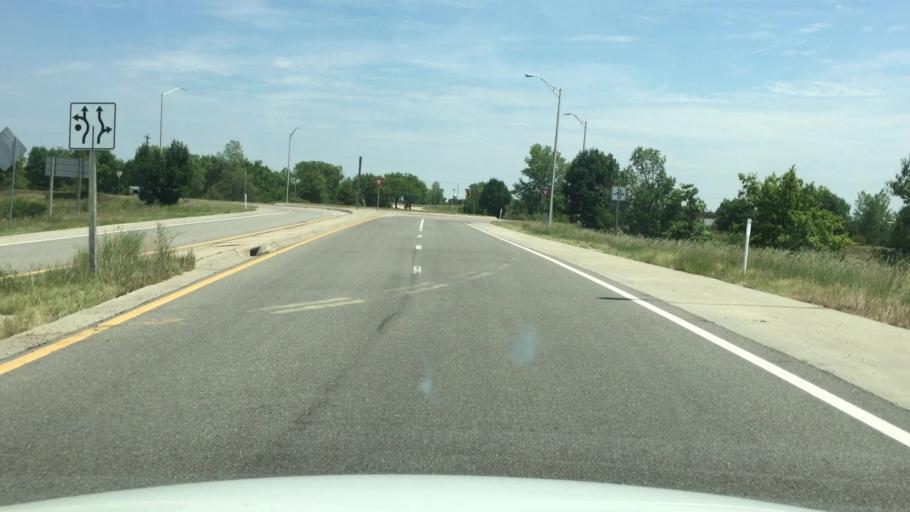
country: US
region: Kansas
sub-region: Shawnee County
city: Topeka
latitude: 39.0318
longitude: -95.6247
